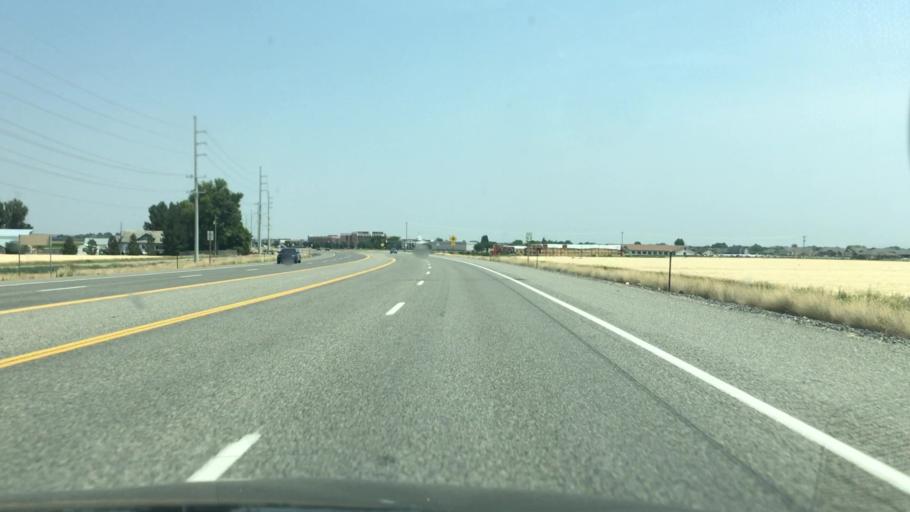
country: US
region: Idaho
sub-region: Twin Falls County
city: Twin Falls
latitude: 42.5921
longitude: -114.5133
